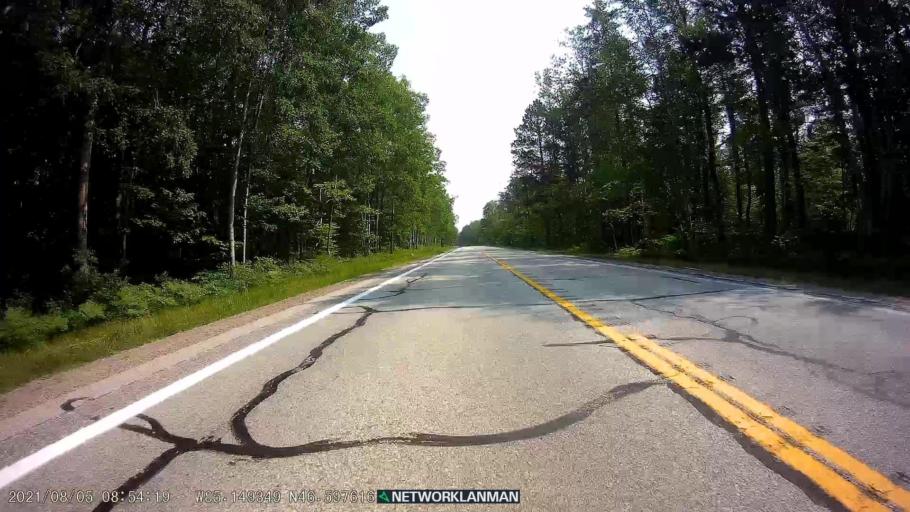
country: US
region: Michigan
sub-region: Luce County
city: Newberry
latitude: 46.5975
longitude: -85.1496
